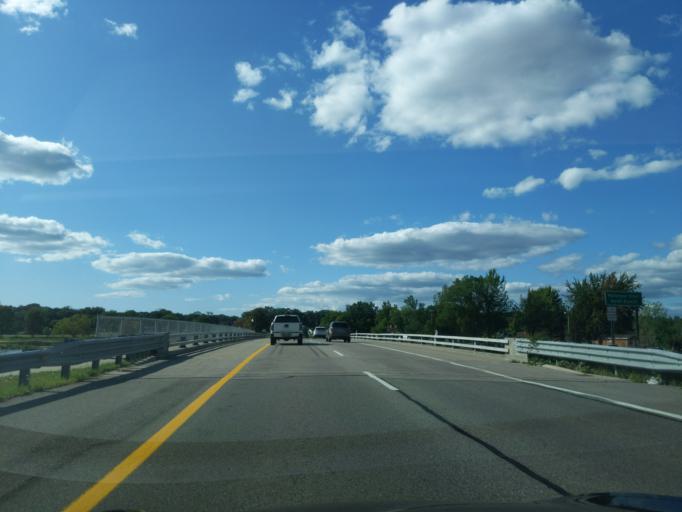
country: US
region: Michigan
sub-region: Muskegon County
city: North Muskegon
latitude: 43.2626
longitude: -86.2447
